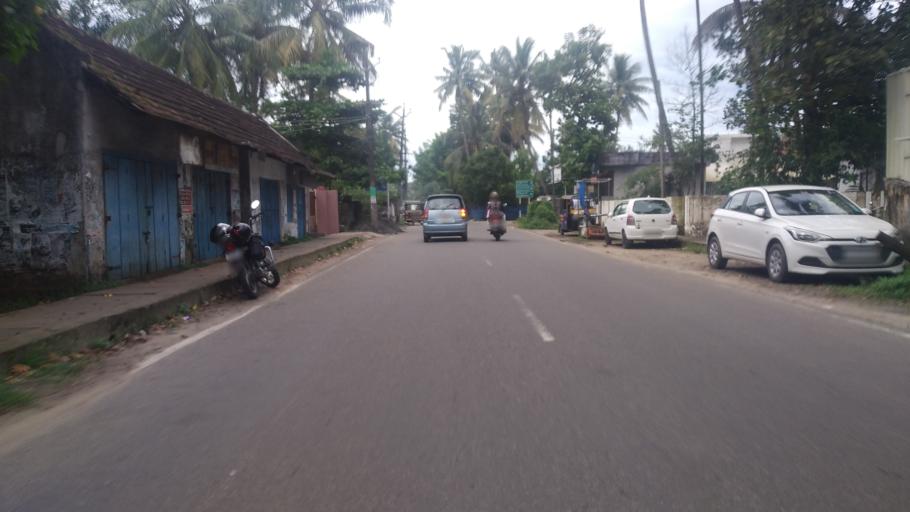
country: IN
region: Kerala
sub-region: Ernakulam
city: Cochin
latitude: 9.9328
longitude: 76.2468
